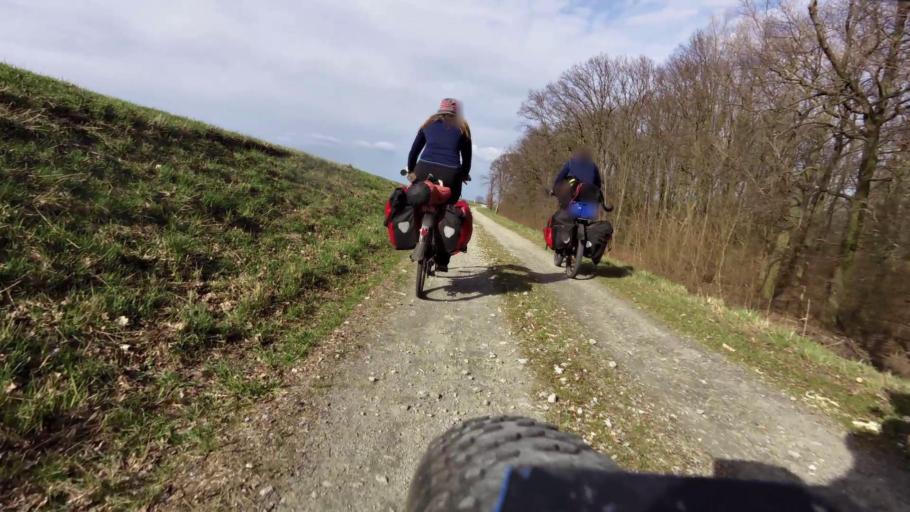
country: DE
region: Brandenburg
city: Reitwein
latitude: 52.5304
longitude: 14.6108
